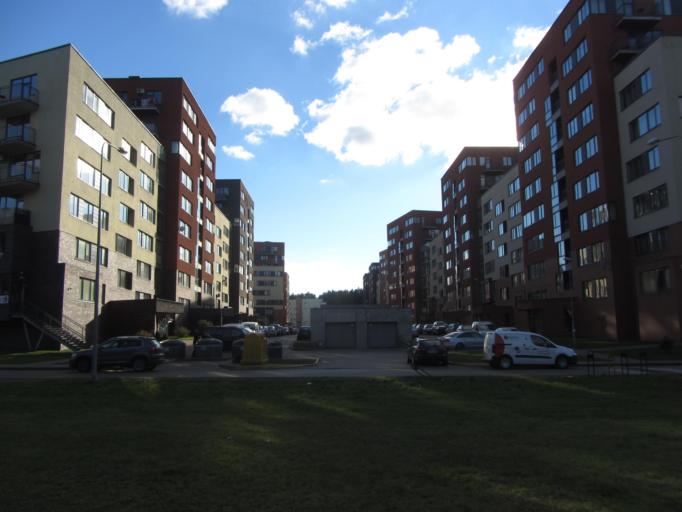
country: LT
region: Vilnius County
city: Lazdynai
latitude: 54.6691
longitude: 25.2125
